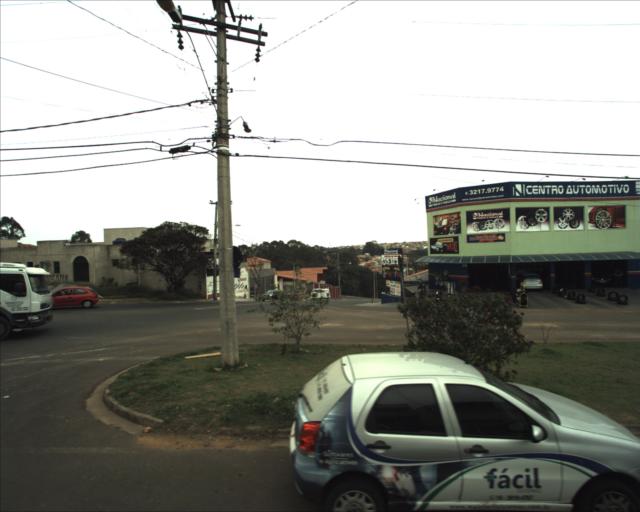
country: BR
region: Sao Paulo
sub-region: Sorocaba
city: Sorocaba
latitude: -23.4927
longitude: -47.5139
